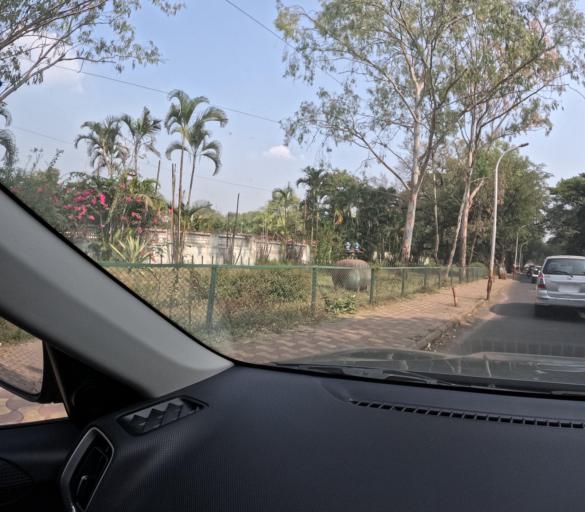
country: IN
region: Maharashtra
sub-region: Pune Division
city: Pune
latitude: 18.5233
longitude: 73.8861
